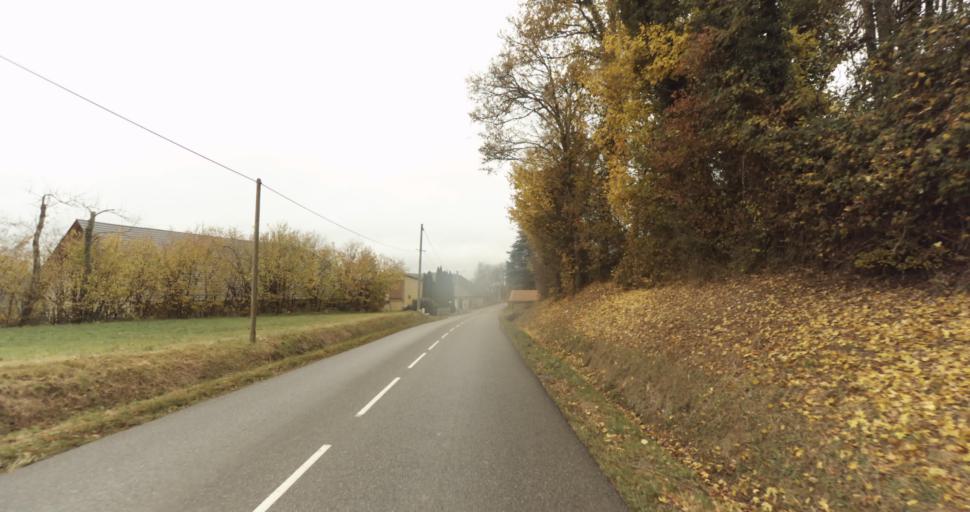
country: FR
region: Rhone-Alpes
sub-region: Departement de la Haute-Savoie
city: Evires
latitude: 46.0338
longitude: 6.2088
